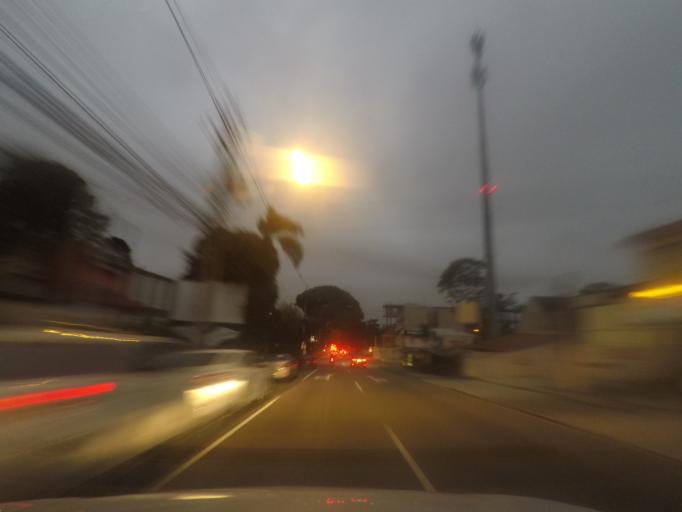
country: BR
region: Parana
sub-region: Curitiba
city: Curitiba
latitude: -25.4232
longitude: -49.2438
